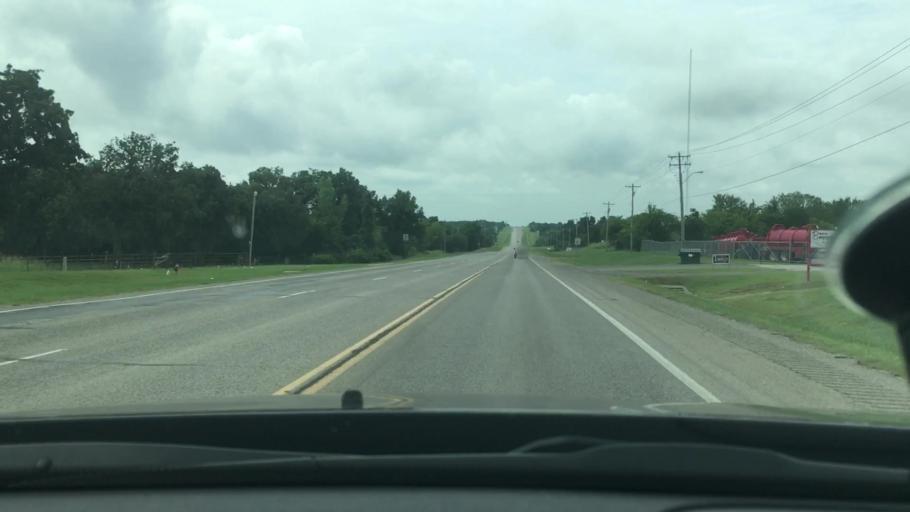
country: US
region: Oklahoma
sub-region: Carter County
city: Healdton
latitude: 34.2141
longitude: -97.4748
